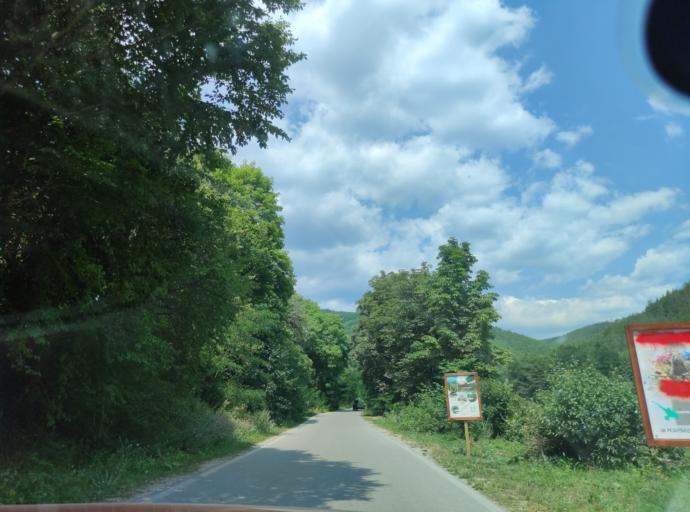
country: BG
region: Blagoevgrad
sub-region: Obshtina Belitsa
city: Belitsa
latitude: 41.9979
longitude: 23.5495
